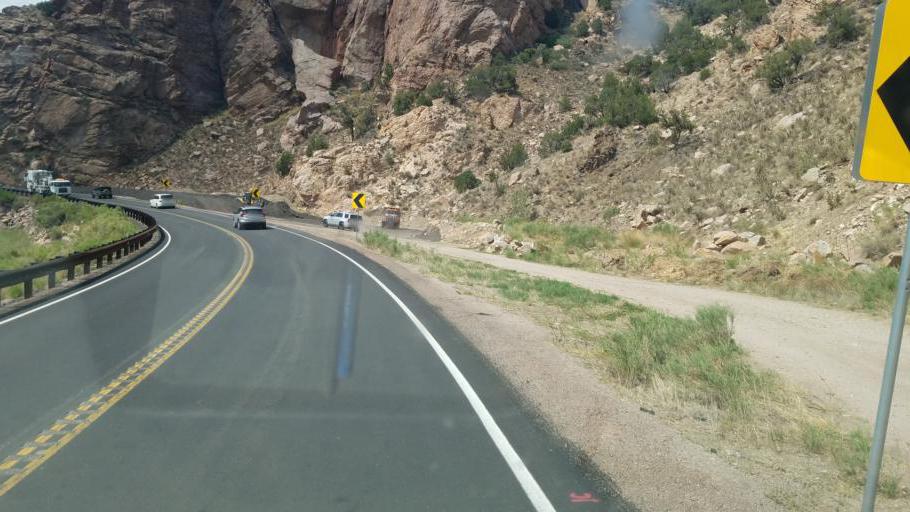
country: US
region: Colorado
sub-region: Fremont County
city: Canon City
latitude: 38.4373
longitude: -105.5390
